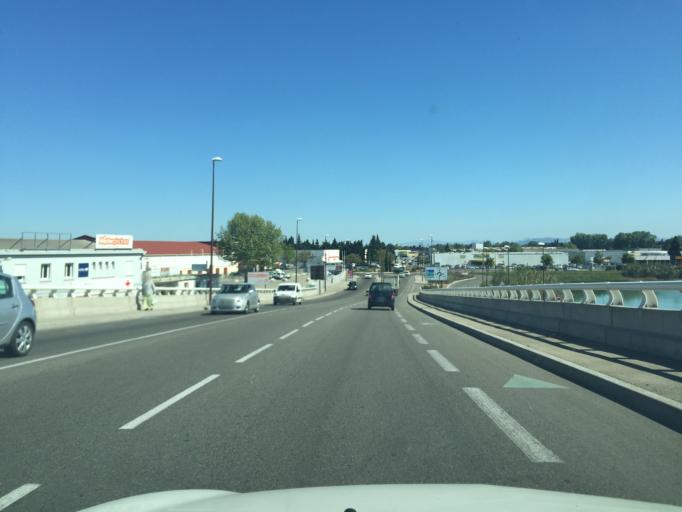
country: FR
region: Provence-Alpes-Cote d'Azur
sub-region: Departement du Vaucluse
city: Montfavet
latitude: 43.9336
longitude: 4.8476
